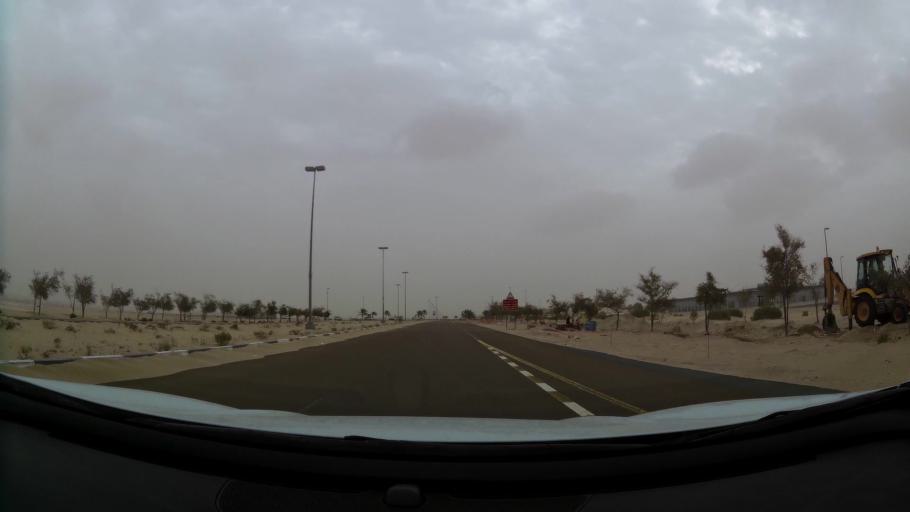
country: AE
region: Abu Dhabi
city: Abu Dhabi
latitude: 24.4254
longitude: 54.7105
